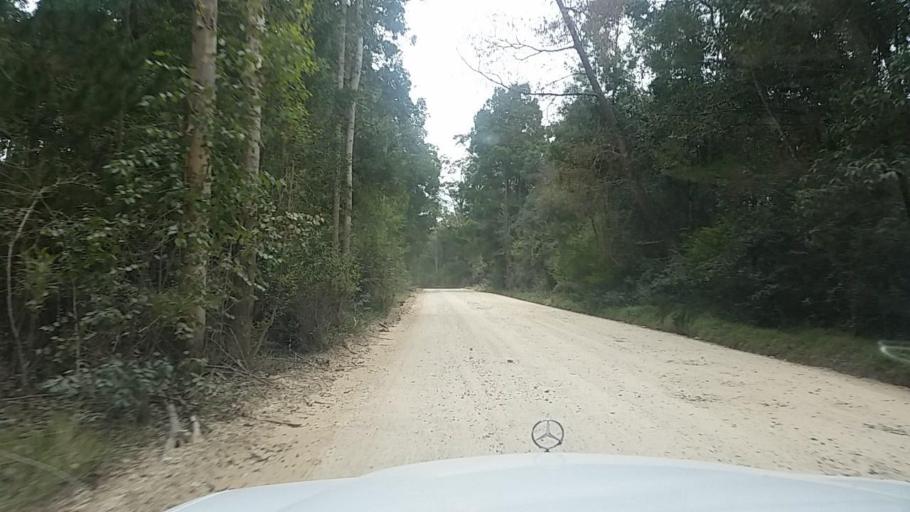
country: ZA
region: Western Cape
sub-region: Eden District Municipality
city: Knysna
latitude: -33.9972
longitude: 23.1310
